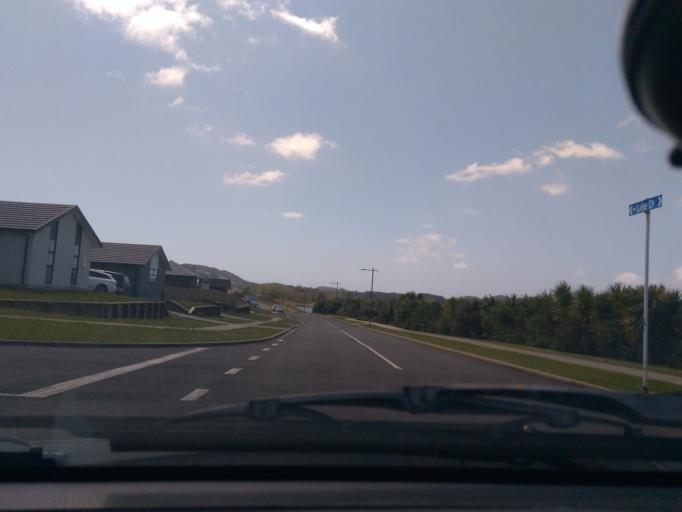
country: NZ
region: Northland
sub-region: Whangarei
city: Whangarei
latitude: -35.6771
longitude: 174.3174
